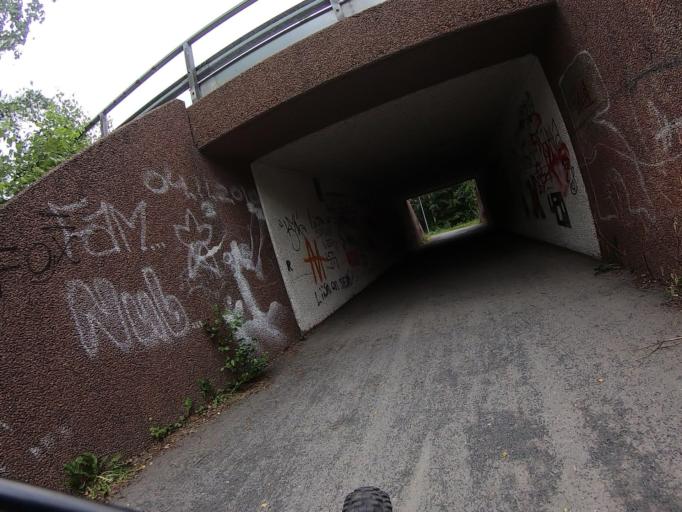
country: FI
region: Varsinais-Suomi
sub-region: Vakka-Suomi
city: Uusikaupunki
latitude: 60.8182
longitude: 21.4138
